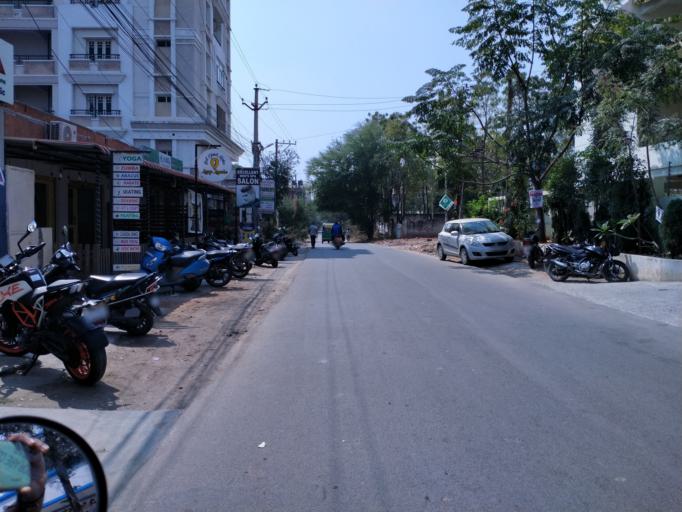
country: IN
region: Telangana
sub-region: Rangareddi
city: Secunderabad
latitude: 17.4997
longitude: 78.5467
